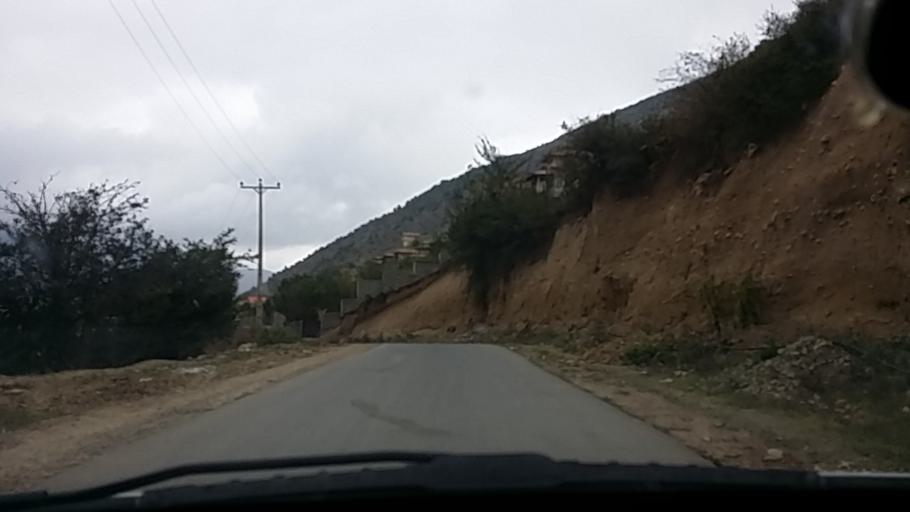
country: IR
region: Mazandaran
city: `Abbasabad
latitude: 36.4713
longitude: 51.1401
